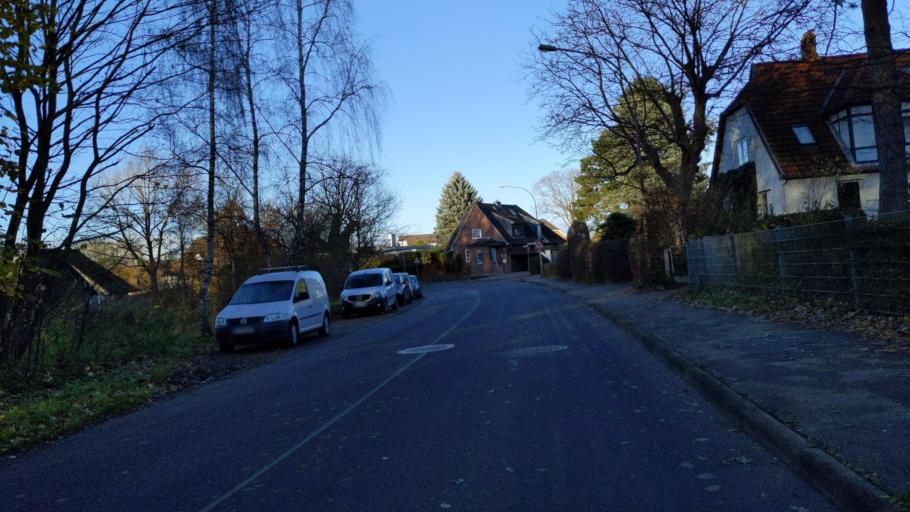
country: DE
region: Schleswig-Holstein
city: Ratekau
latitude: 53.8999
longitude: 10.7452
